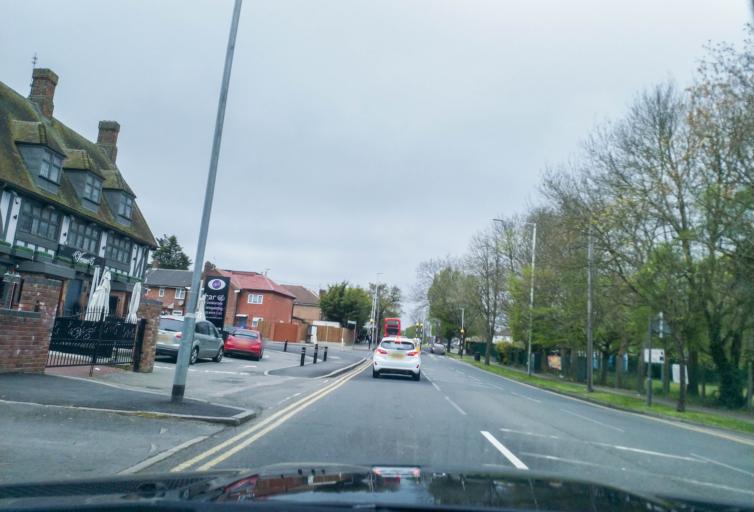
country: GB
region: England
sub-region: Greater London
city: Pinner
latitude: 51.5689
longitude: -0.3892
